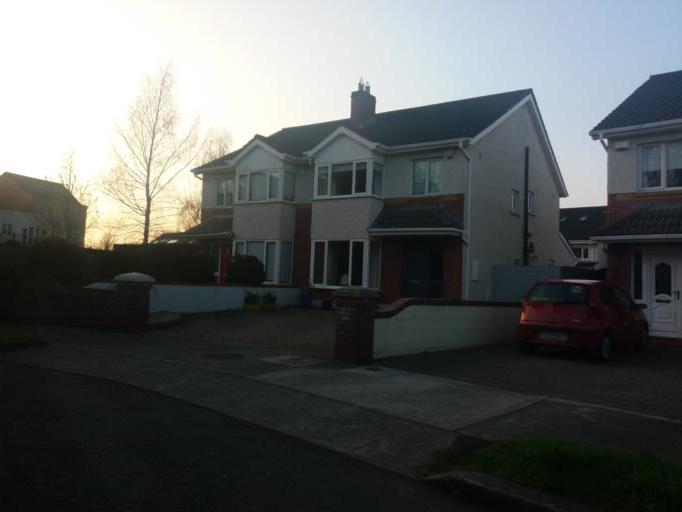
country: IE
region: Leinster
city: Hartstown
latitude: 53.3878
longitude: -6.4288
